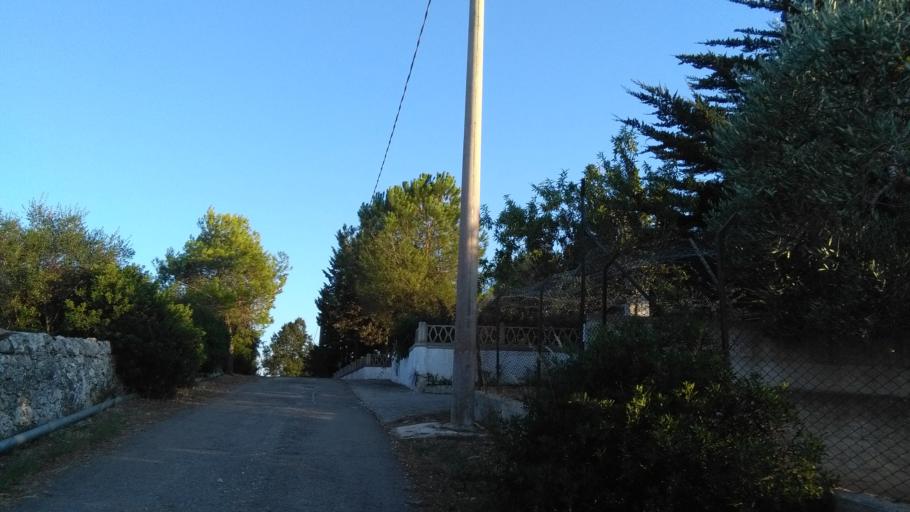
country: IT
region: Apulia
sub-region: Provincia di Bari
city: Putignano
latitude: 40.8282
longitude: 17.0769
